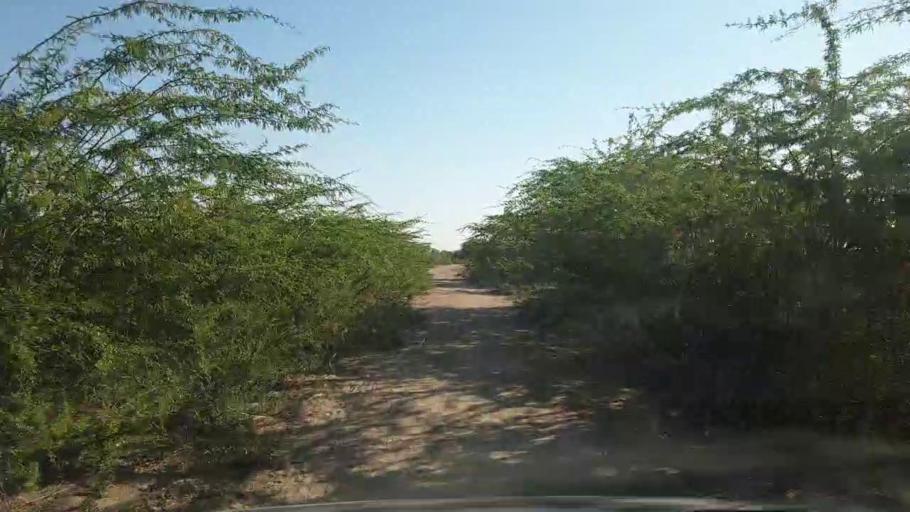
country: PK
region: Sindh
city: Dhoro Naro
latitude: 25.4123
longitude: 69.5688
